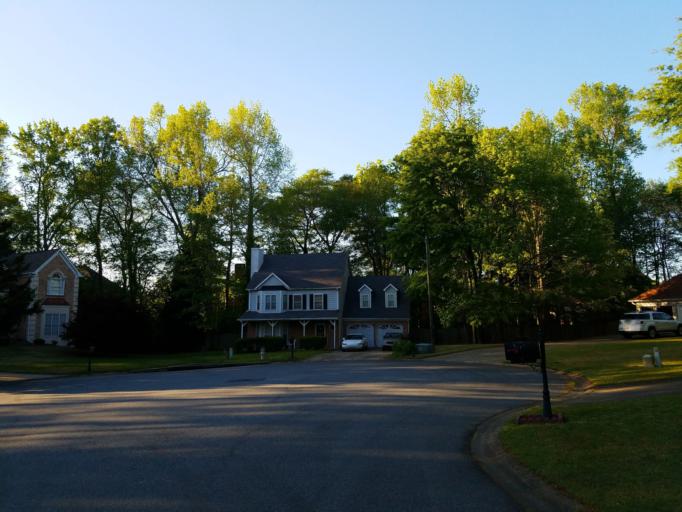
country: US
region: Georgia
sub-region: Cobb County
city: Powder Springs
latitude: 33.9235
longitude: -84.6387
